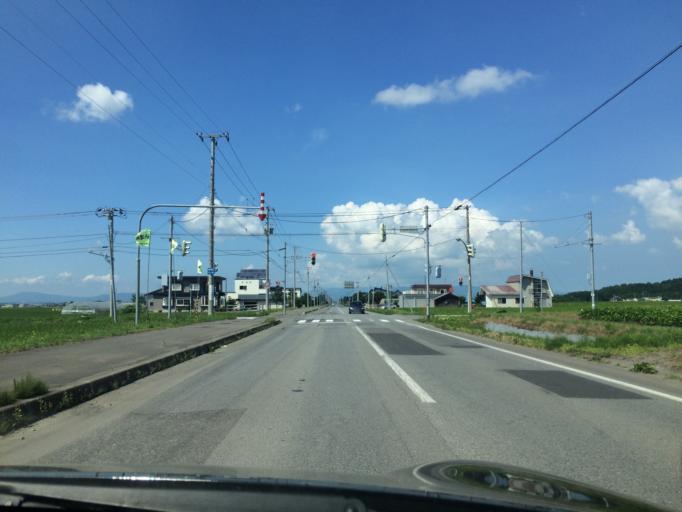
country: JP
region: Hokkaido
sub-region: Asahikawa-shi
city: Asahikawa
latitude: 43.7565
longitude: 142.4628
